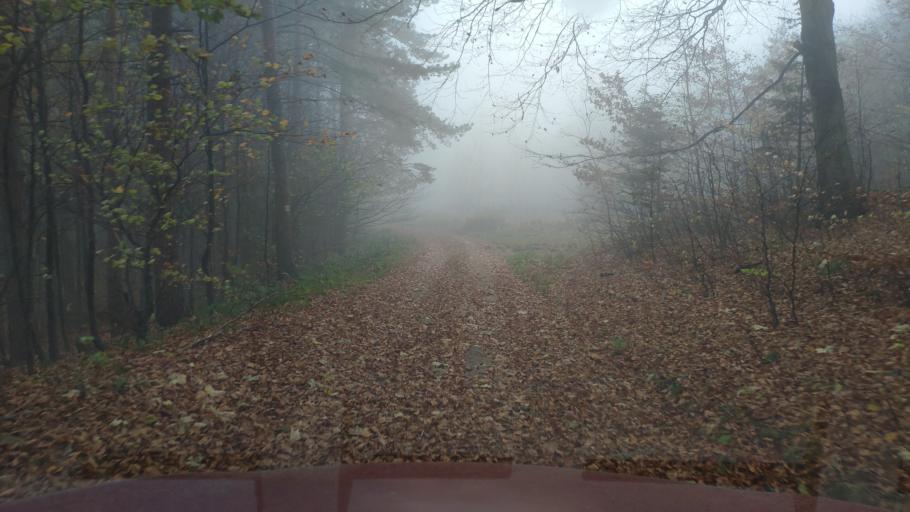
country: SK
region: Presovsky
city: Sabinov
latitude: 49.1547
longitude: 21.2253
